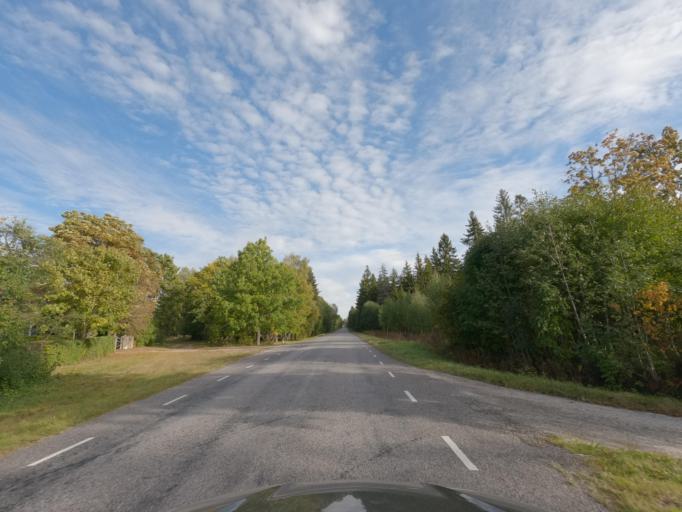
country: EE
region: Raplamaa
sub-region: Kohila vald
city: Kohila
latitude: 59.1057
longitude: 24.6817
